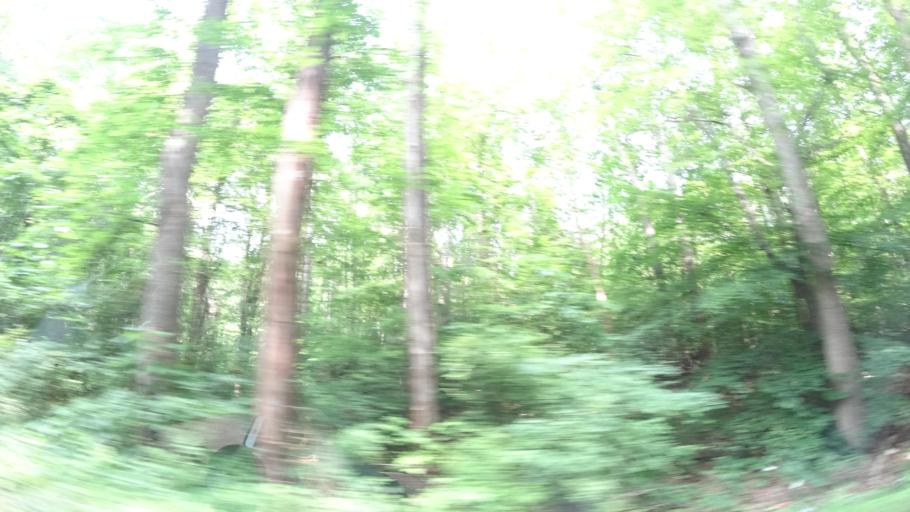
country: US
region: Virginia
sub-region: Spotsylvania County
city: Spotsylvania Courthouse
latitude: 38.1583
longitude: -77.6357
